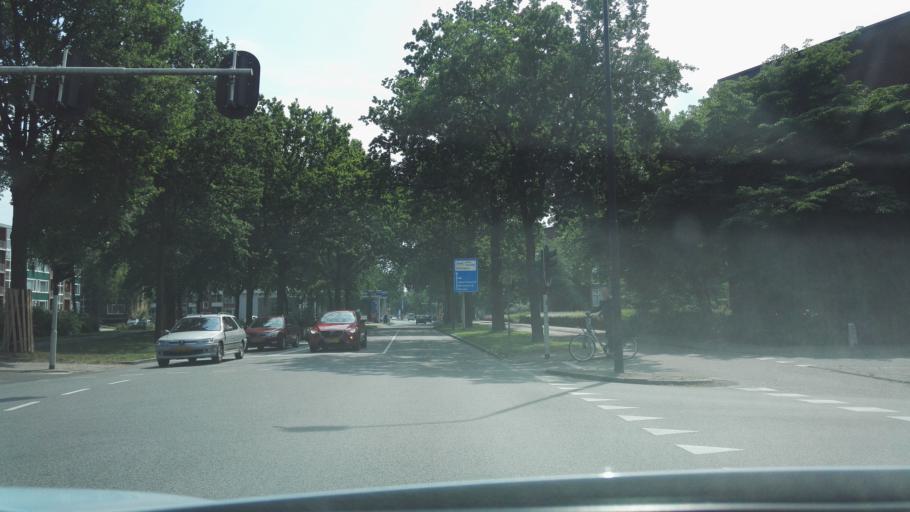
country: NL
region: Gelderland
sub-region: Gemeente Apeldoorn
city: Apeldoorn
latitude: 52.1938
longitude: 5.9741
